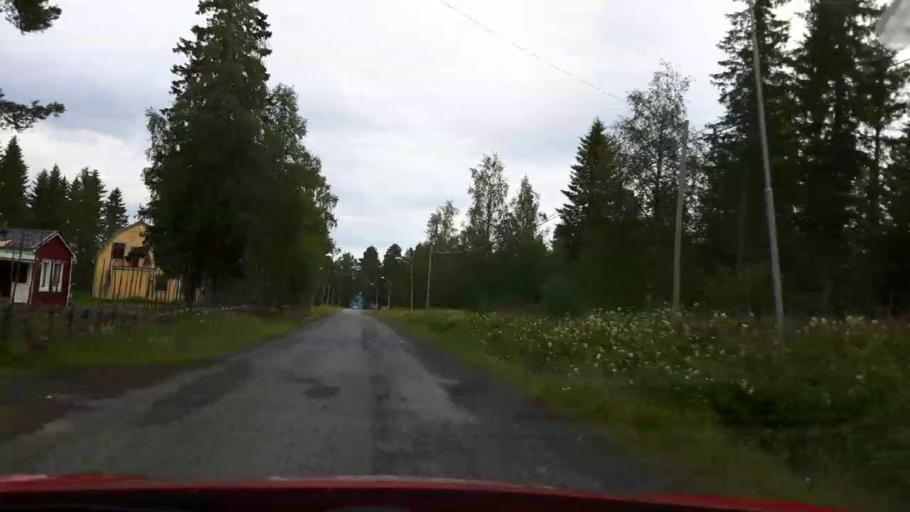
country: SE
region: Jaemtland
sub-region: Stroemsunds Kommun
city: Stroemsund
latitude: 63.5196
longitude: 15.3505
